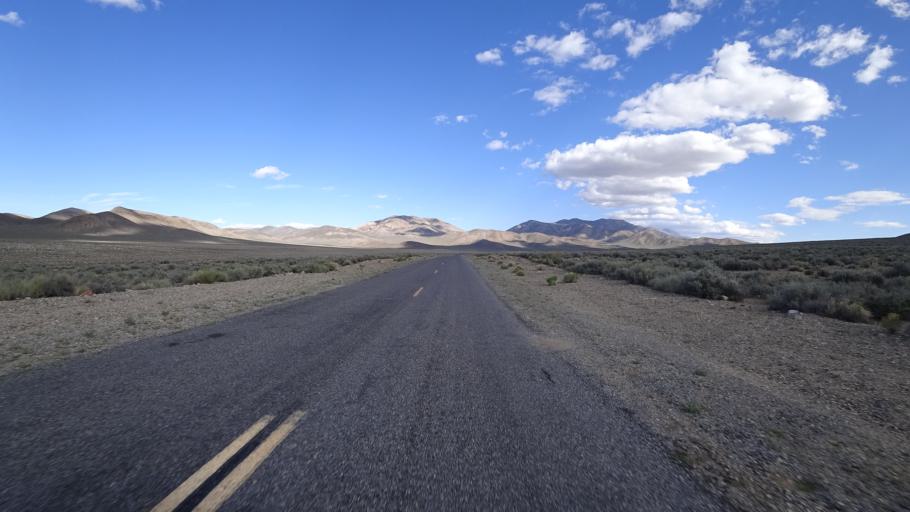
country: US
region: Nevada
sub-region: Nye County
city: Beatty
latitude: 36.3807
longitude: -117.1468
